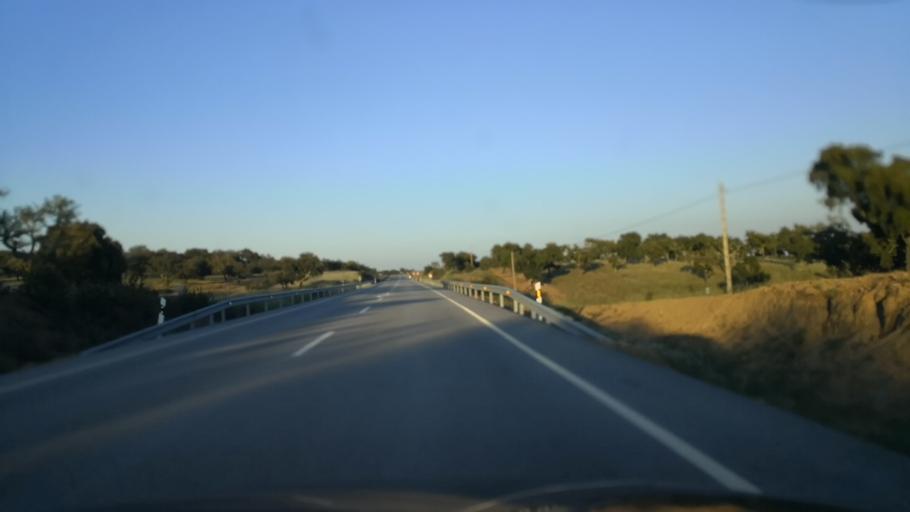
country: ES
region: Extremadura
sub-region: Provincia de Caceres
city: Carbajo
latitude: 39.5072
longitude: -7.1269
